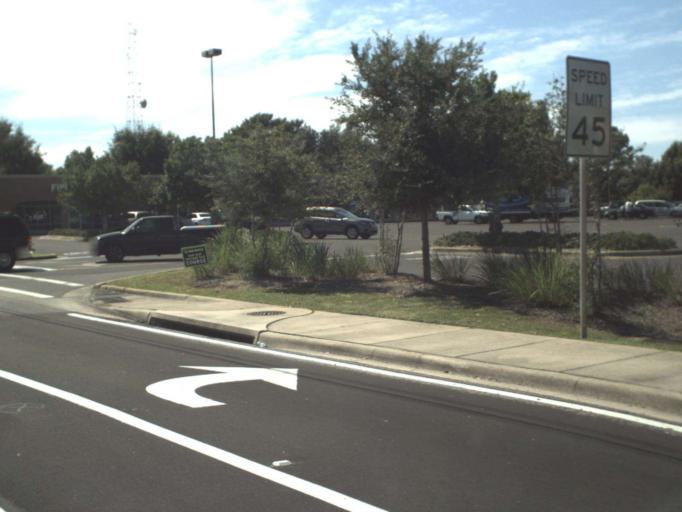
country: US
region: Florida
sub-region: Okaloosa County
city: Wright
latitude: 30.4477
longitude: -86.6387
